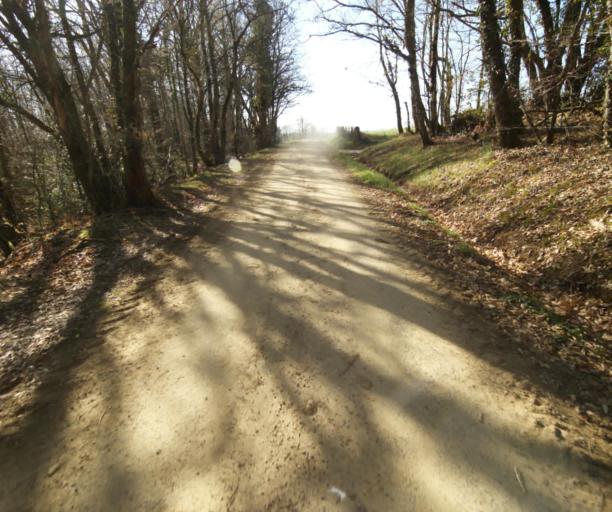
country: FR
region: Limousin
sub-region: Departement de la Correze
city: Seilhac
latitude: 45.3767
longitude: 1.7648
